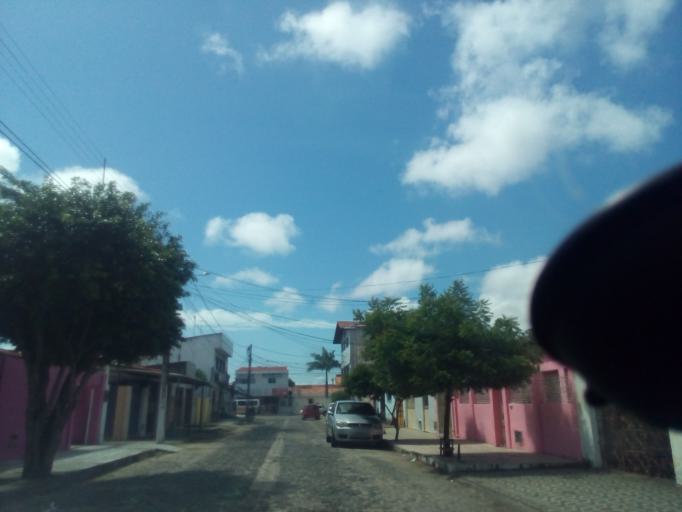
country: BR
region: Rio Grande do Norte
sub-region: Natal
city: Natal
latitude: -5.8257
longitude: -35.2384
